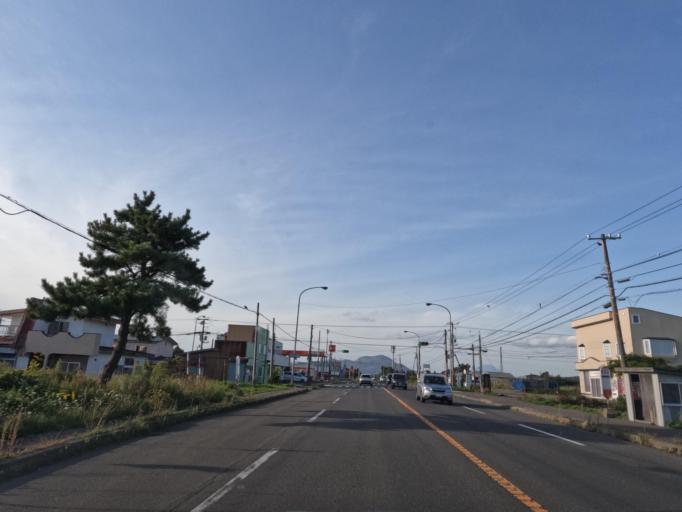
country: JP
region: Hokkaido
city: Date
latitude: 42.4274
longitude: 140.9053
